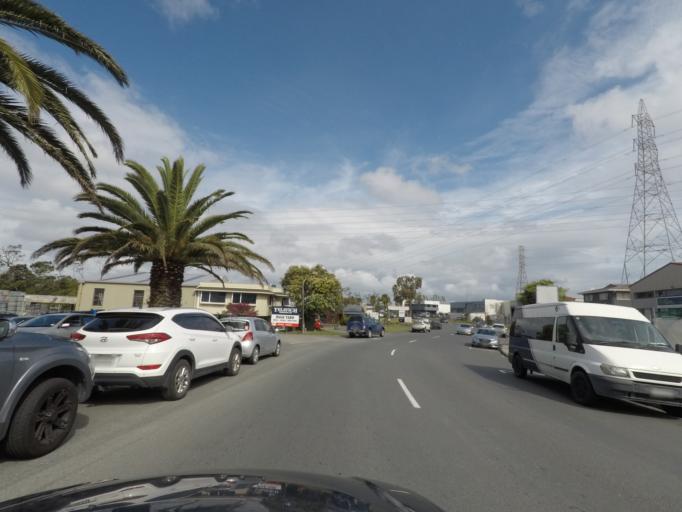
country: NZ
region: Auckland
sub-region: Auckland
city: Rosebank
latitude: -36.8472
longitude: 174.6333
